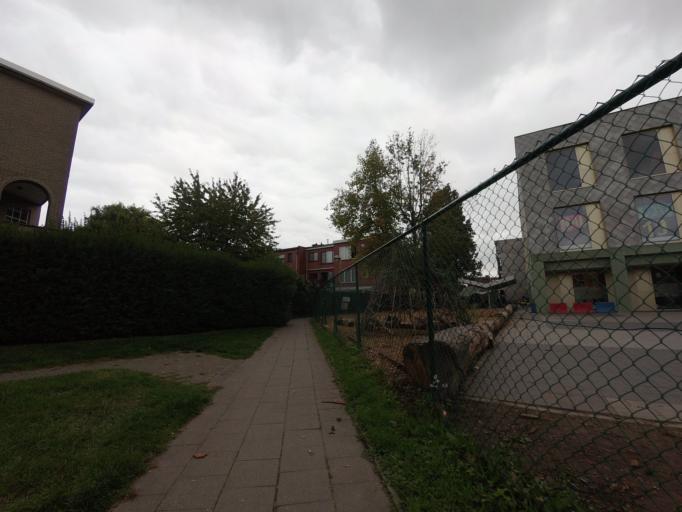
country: BE
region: Flanders
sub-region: Provincie Antwerpen
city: Antwerpen
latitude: 51.2492
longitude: 4.4362
